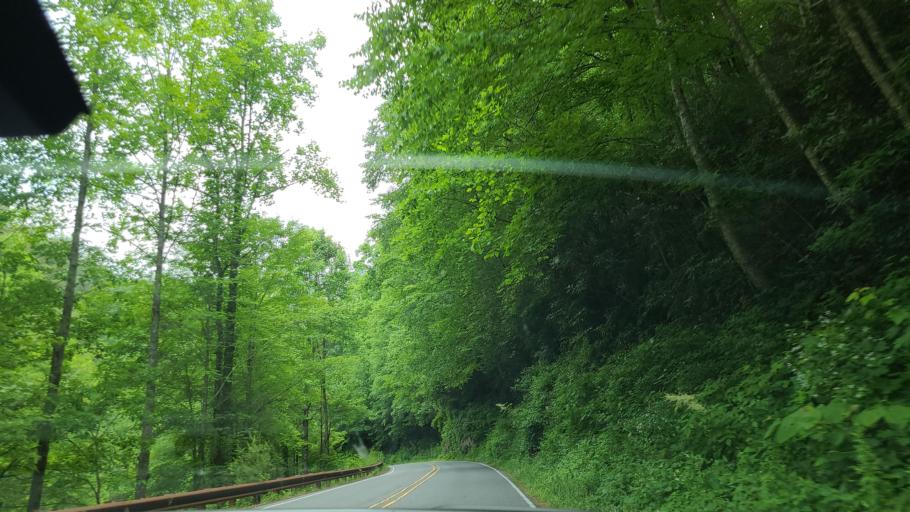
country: US
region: North Carolina
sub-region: Macon County
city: Franklin
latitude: 35.0904
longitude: -83.2679
